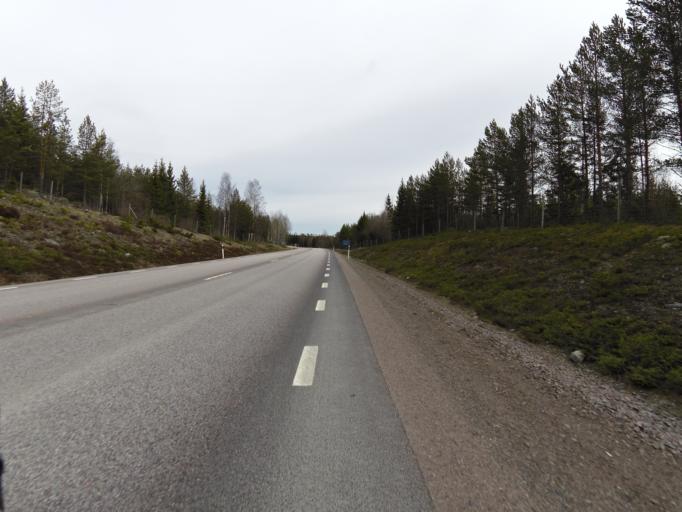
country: SE
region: Gaevleborg
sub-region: Hofors Kommun
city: Hofors
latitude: 60.5407
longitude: 16.1884
